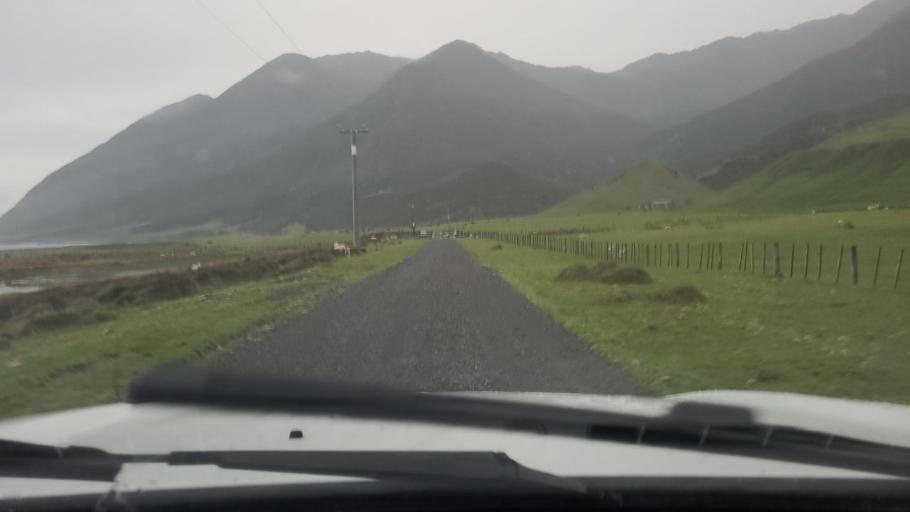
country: NZ
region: Wellington
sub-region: South Wairarapa District
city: Waipawa
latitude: -41.5682
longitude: 175.3765
